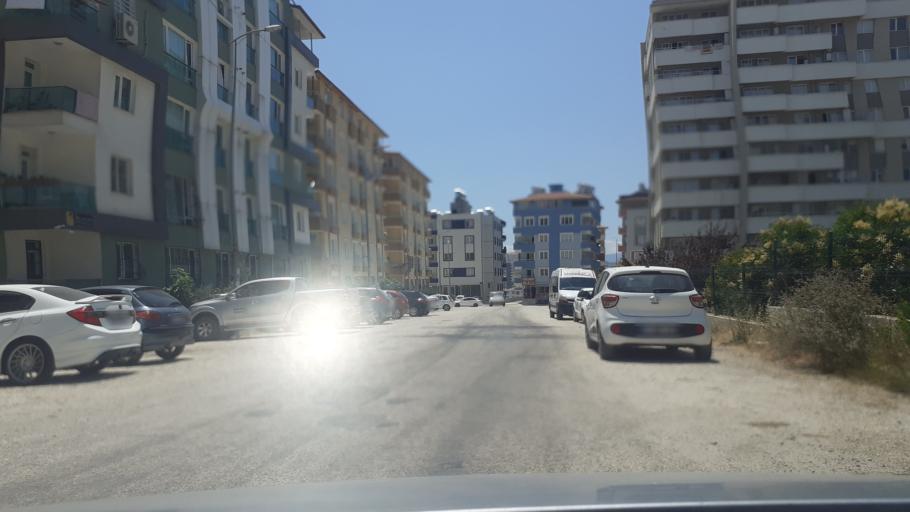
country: TR
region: Hatay
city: Gunyazi
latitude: 36.2349
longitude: 36.1381
